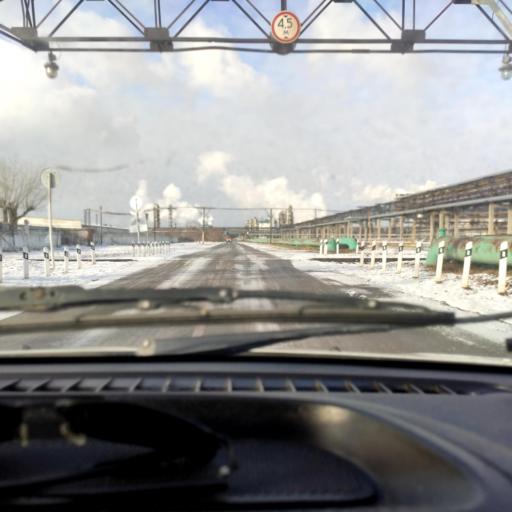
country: RU
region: Samara
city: Tol'yatti
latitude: 53.5355
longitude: 49.4742
